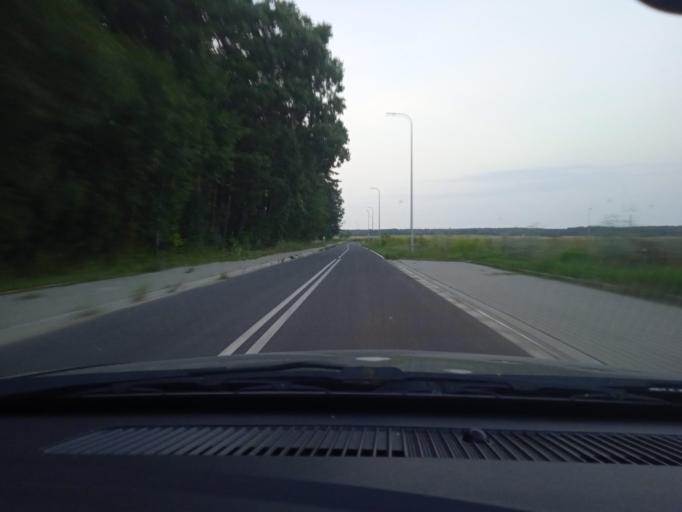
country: PL
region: Masovian Voivodeship
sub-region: Powiat nowodworski
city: Pomiechowek
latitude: 52.4775
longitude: 20.6979
